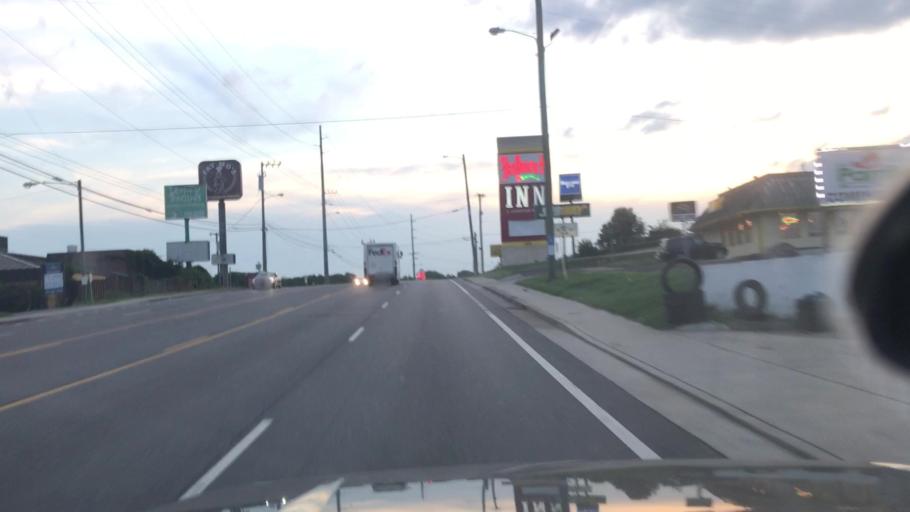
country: US
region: Tennessee
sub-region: Davidson County
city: Nashville
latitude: 36.2068
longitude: -86.7792
